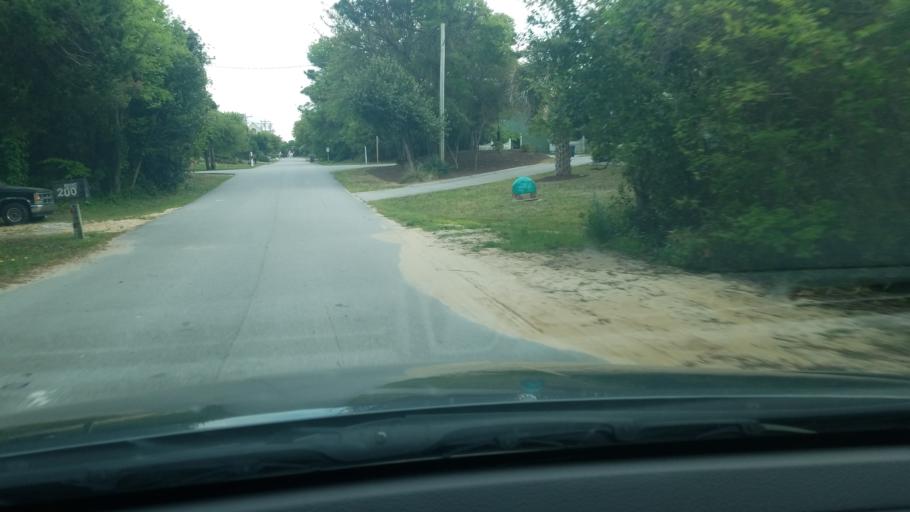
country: US
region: North Carolina
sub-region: Carteret County
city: Cape Carteret
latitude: 34.6678
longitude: -77.0170
